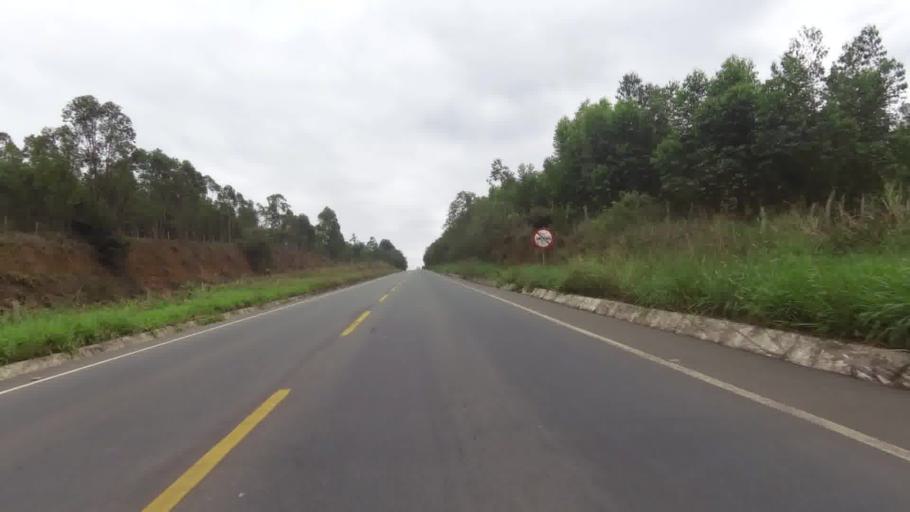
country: BR
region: Espirito Santo
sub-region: Piuma
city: Piuma
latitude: -20.7932
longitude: -40.7506
